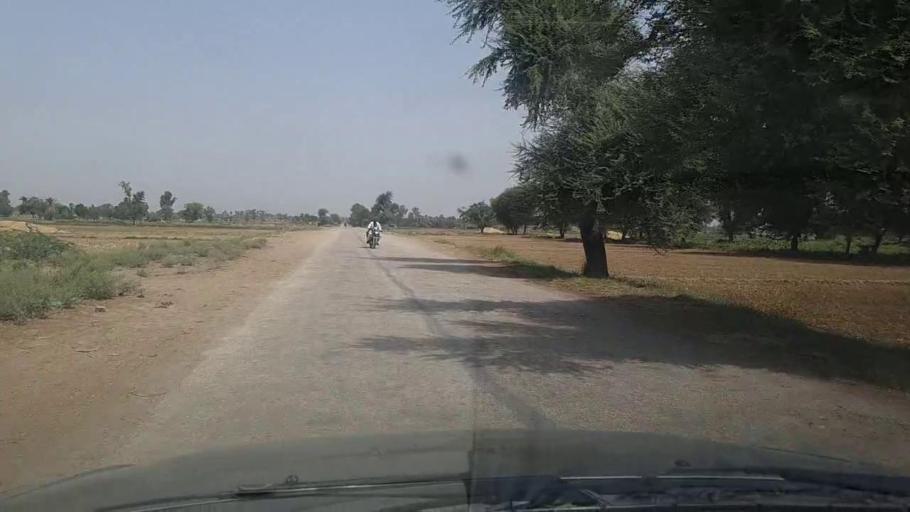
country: PK
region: Sindh
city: Setharja Old
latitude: 27.1570
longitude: 68.5205
